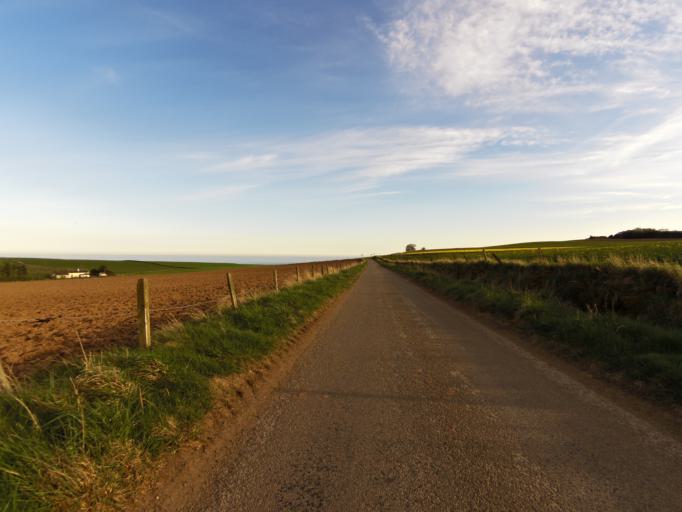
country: GB
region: Scotland
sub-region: Aberdeenshire
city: Inverbervie
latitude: 56.8801
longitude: -2.2358
